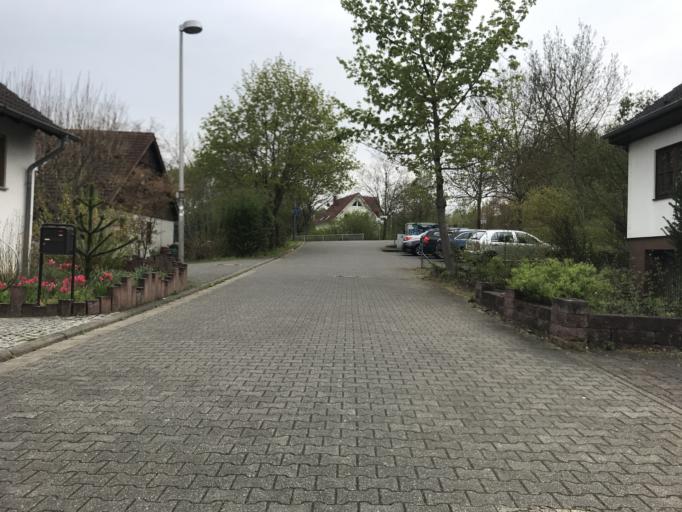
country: DE
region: Rheinland-Pfalz
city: Gau-Algesheim
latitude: 49.9486
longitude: 8.0152
